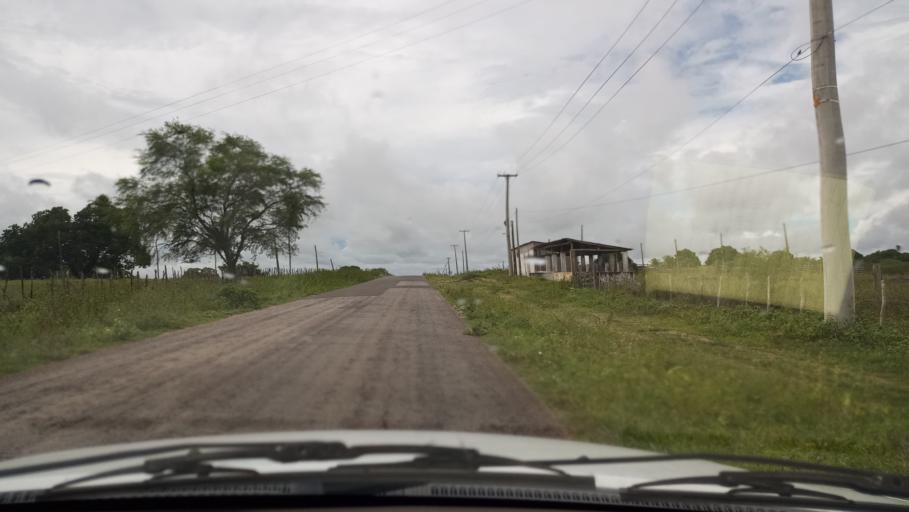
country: BR
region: Rio Grande do Norte
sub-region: Poco Branco
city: Poco Branco
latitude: -5.6141
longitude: -35.6479
